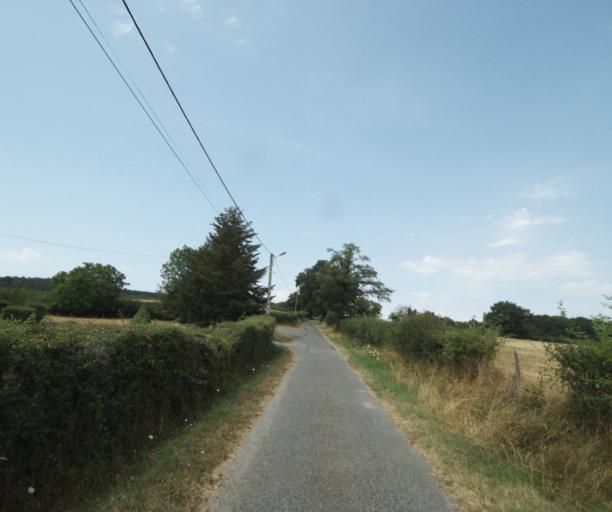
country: FR
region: Bourgogne
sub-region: Departement de Saone-et-Loire
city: Gueugnon
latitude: 46.6014
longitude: 4.0383
